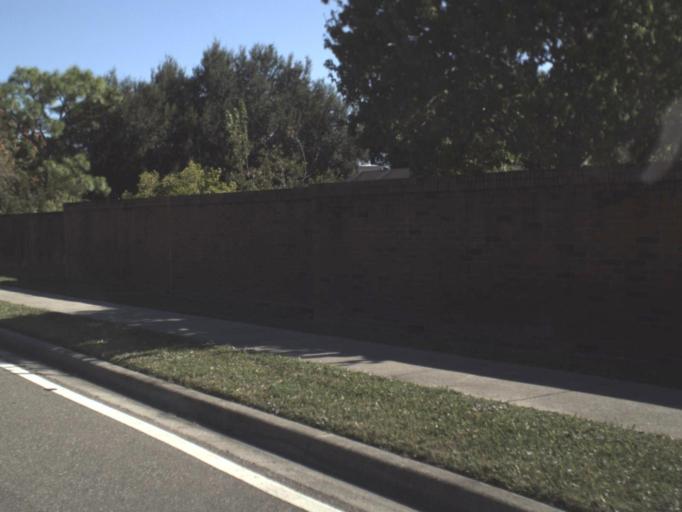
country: US
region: Florida
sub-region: Brevard County
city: South Patrick Shores
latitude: 28.2300
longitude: -80.6847
